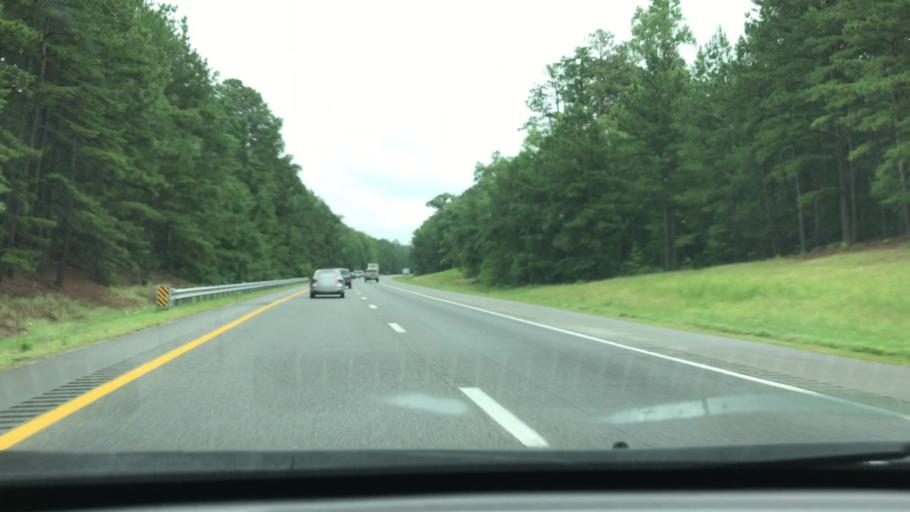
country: US
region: Virginia
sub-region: City of Emporia
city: Emporia
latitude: 36.7515
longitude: -77.5100
